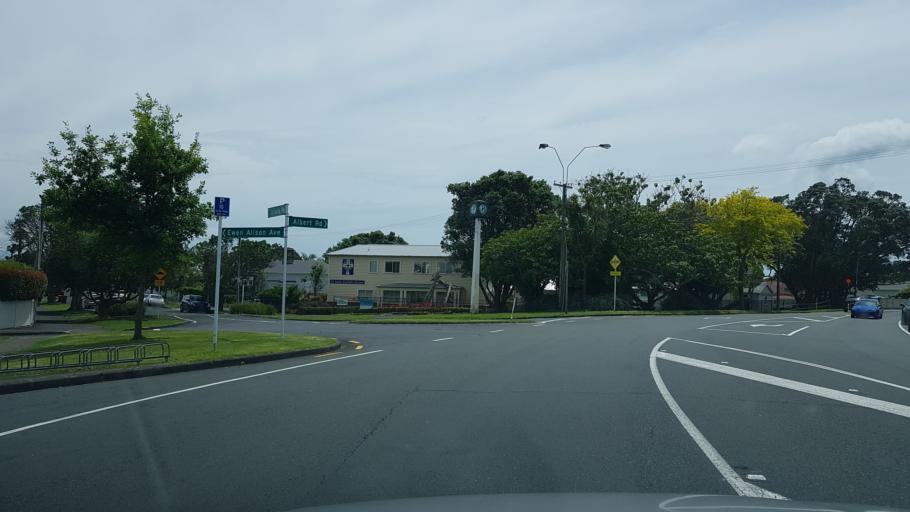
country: NZ
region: Auckland
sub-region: Auckland
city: Auckland
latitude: -36.8261
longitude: 174.7969
